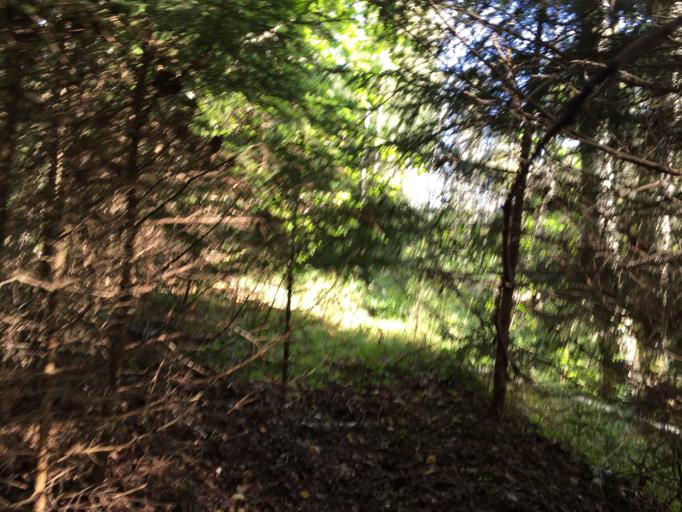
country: LV
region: Kuldigas Rajons
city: Kuldiga
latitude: 57.0034
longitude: 21.7916
